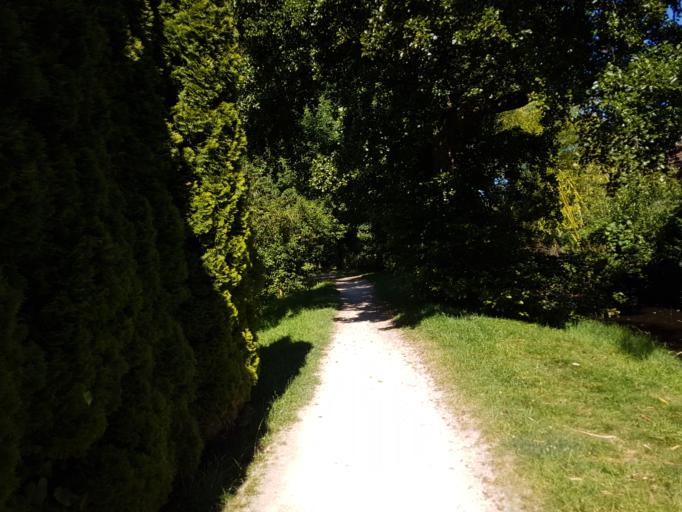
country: FR
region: Franche-Comte
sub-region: Departement de la Haute-Saone
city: Saint-Sauveur
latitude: 47.8154
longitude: 6.3845
